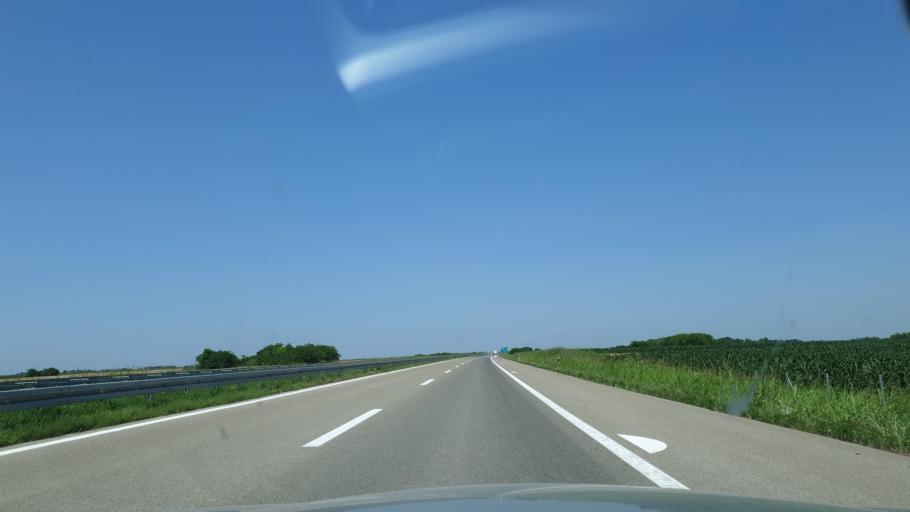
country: RS
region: Autonomna Pokrajina Vojvodina
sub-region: Severnobacki Okrug
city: Backa Topola
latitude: 45.9153
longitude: 19.7022
